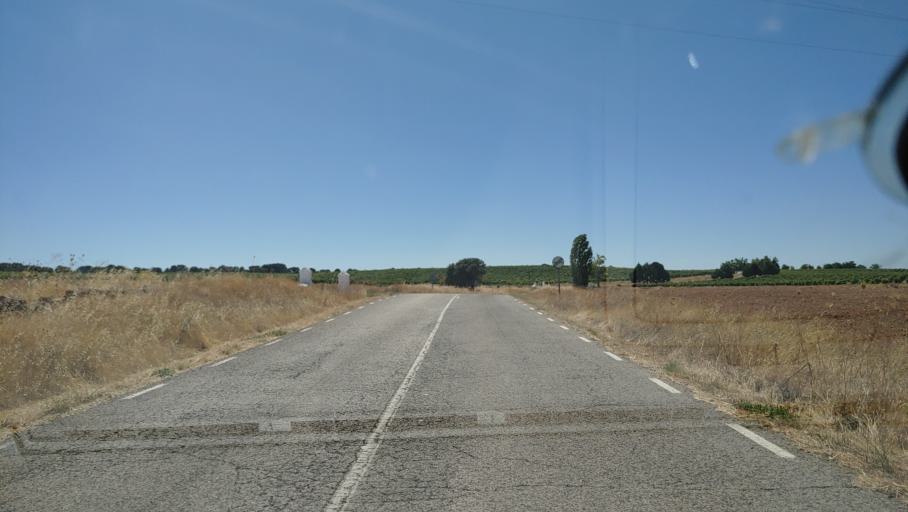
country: ES
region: Castille-La Mancha
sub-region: Provincia de Albacete
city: Ossa de Montiel
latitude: 38.8982
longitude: -2.7627
